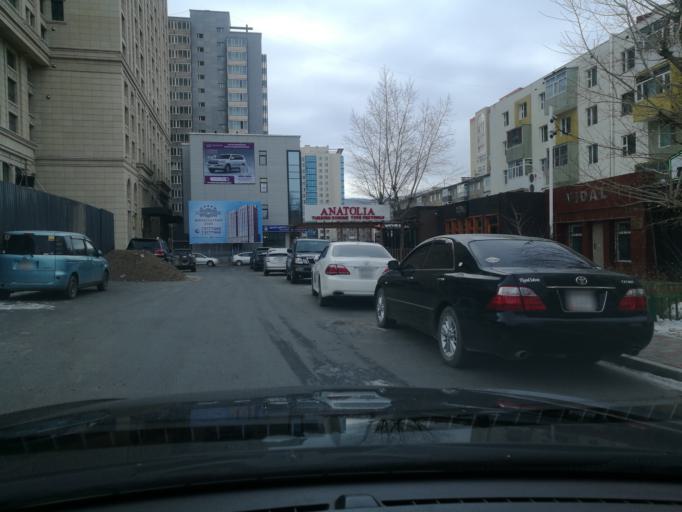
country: MN
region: Ulaanbaatar
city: Ulaanbaatar
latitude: 47.9125
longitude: 106.9059
